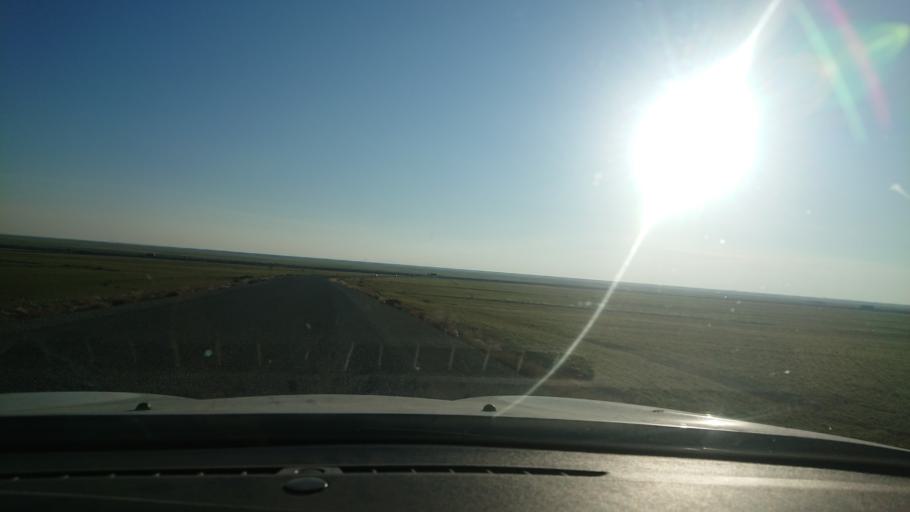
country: TR
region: Aksaray
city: Acipinar
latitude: 38.6675
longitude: 33.7225
